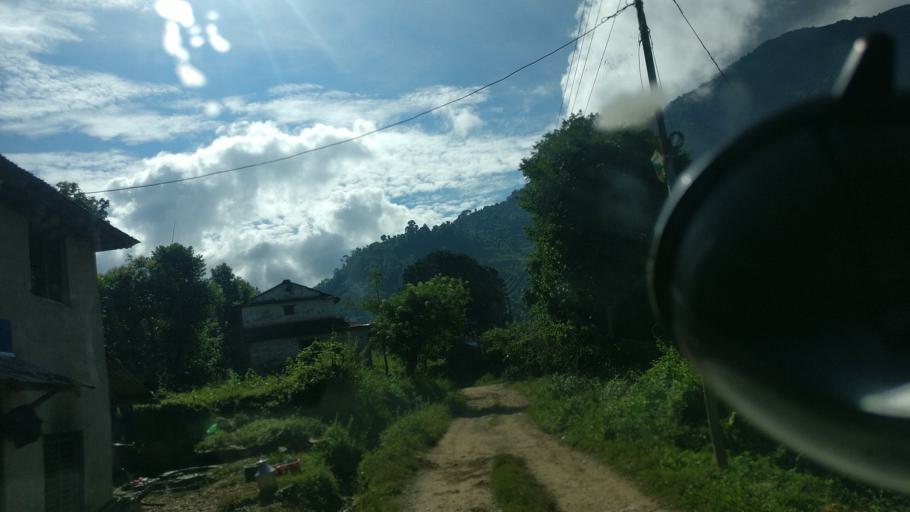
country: NP
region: Western Region
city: Baglung
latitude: 28.1350
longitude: 83.6564
